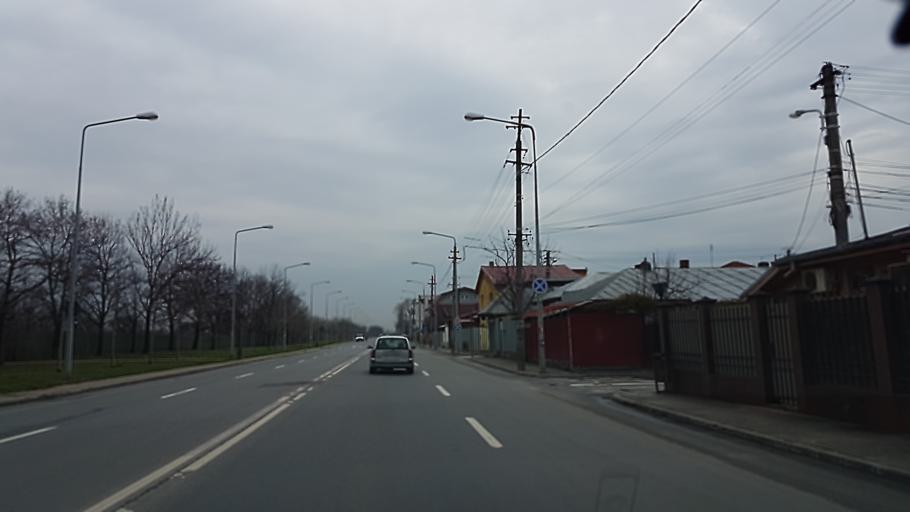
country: RO
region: Ilfov
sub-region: Comuna Pantelimon
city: Pantelimon
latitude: 44.4352
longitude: 26.2029
